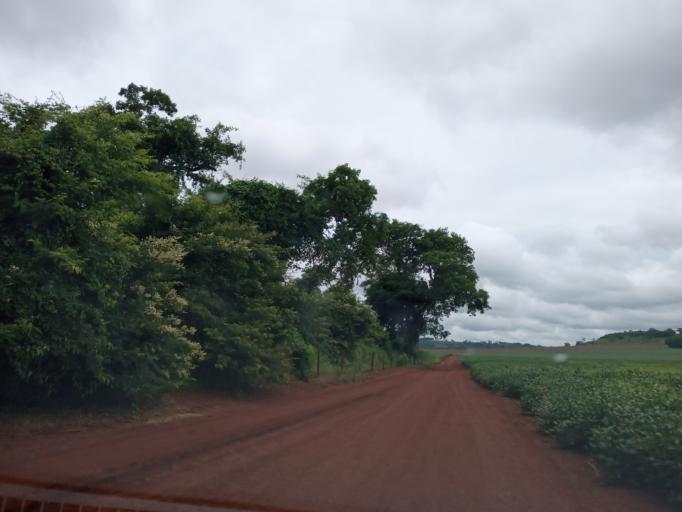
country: BR
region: Minas Gerais
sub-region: Centralina
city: Centralina
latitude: -18.5893
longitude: -49.1453
